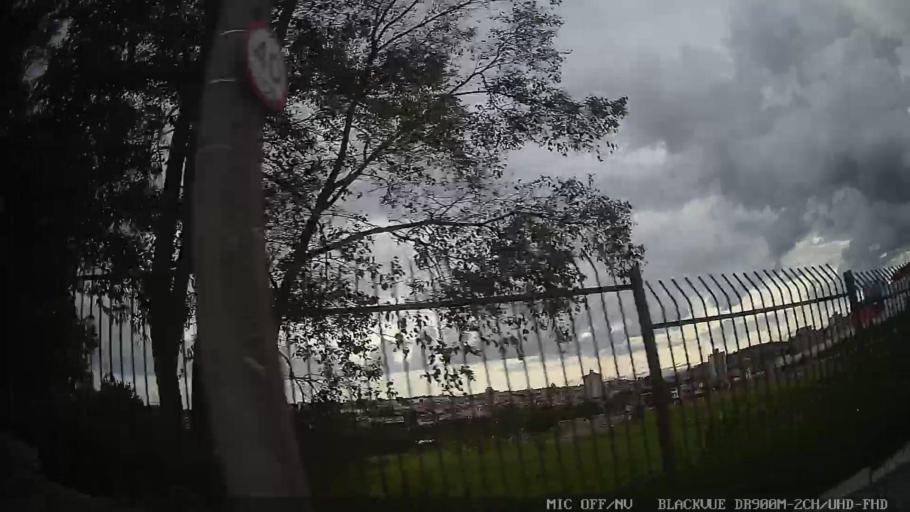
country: BR
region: Sao Paulo
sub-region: Mogi das Cruzes
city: Mogi das Cruzes
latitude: -23.5364
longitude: -46.1979
